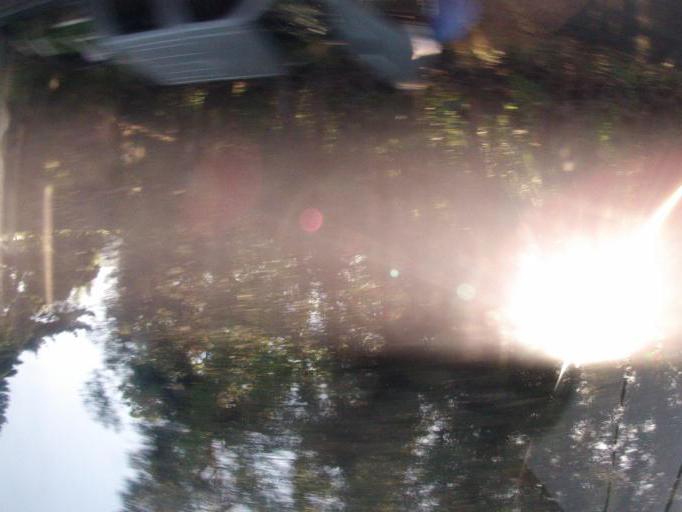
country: CL
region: O'Higgins
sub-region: Provincia de Colchagua
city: Chimbarongo
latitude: -34.7248
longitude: -71.0353
